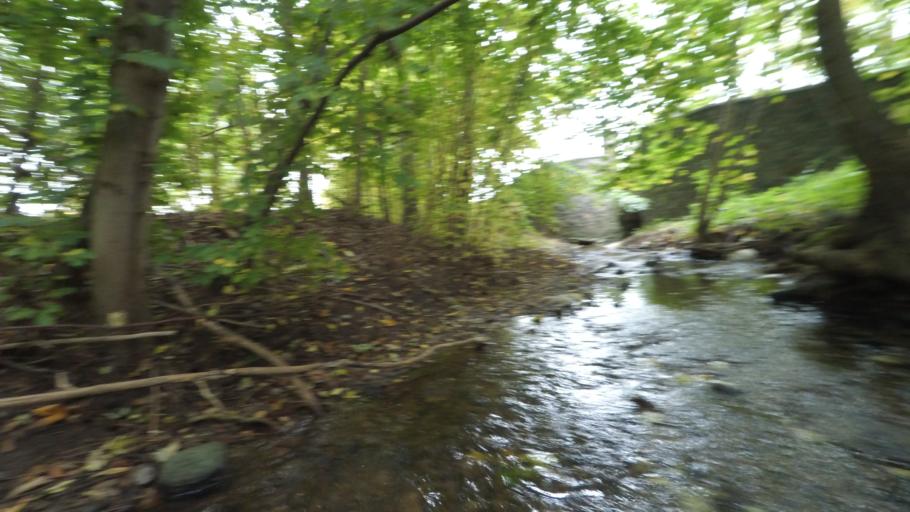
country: DK
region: Central Jutland
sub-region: Arhus Kommune
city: Stavtrup
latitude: 56.1487
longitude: 10.0883
